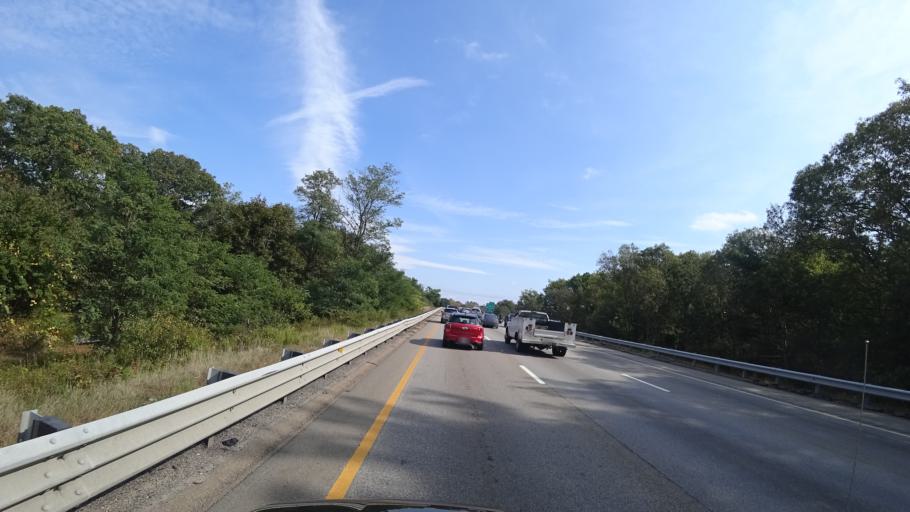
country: US
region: Massachusetts
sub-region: Norfolk County
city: Weymouth
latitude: 42.1877
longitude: -70.9348
